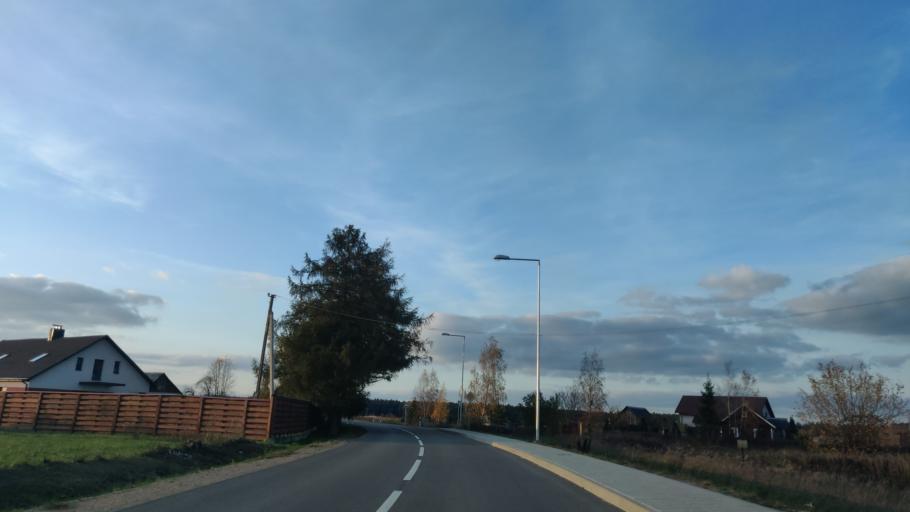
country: LT
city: Lentvaris
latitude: 54.5912
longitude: 25.0484
